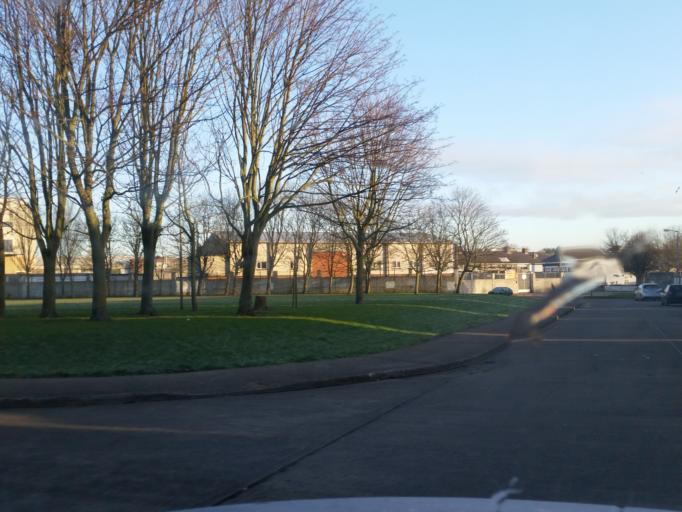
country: IE
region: Leinster
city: Beaumont
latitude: 53.3871
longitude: -6.2506
